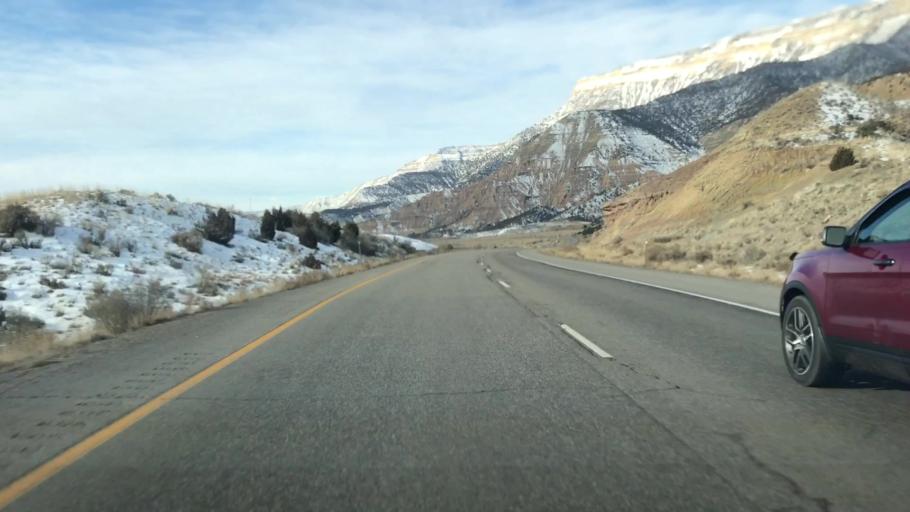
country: US
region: Colorado
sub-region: Garfield County
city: Battlement Mesa
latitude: 39.4992
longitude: -107.9202
